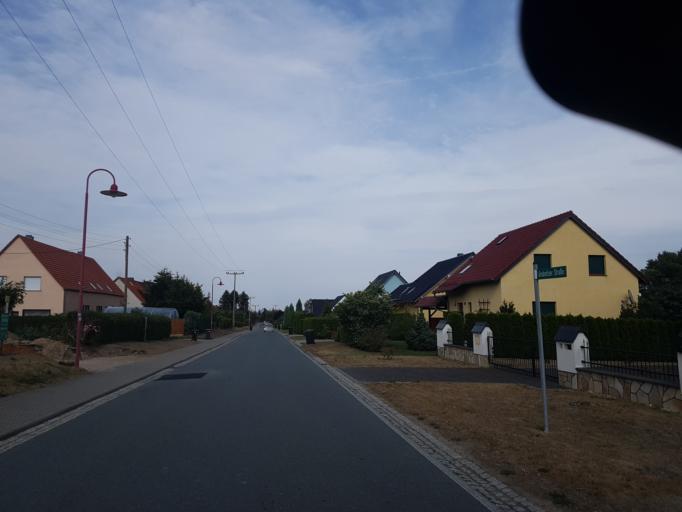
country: DE
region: Saxony
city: Stauchitz
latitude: 51.2640
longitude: 13.2318
